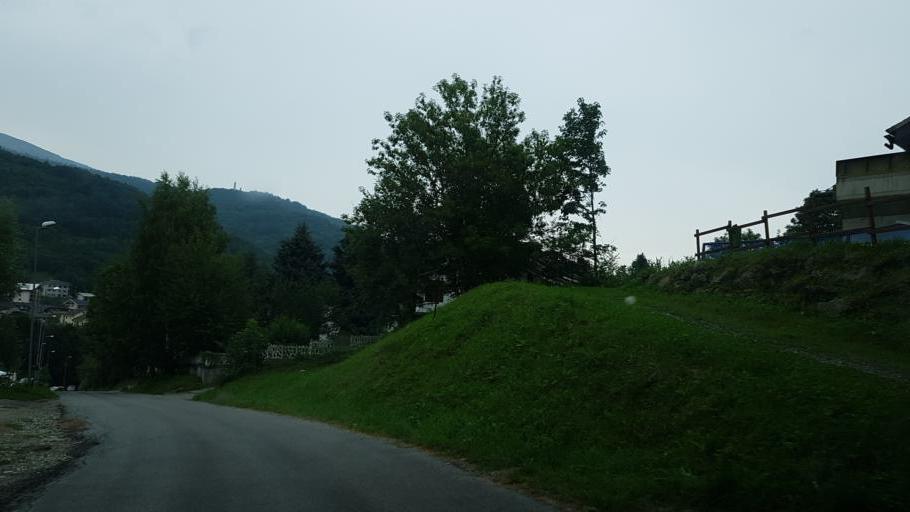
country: IT
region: Piedmont
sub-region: Provincia di Cuneo
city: Sampeyre
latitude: 44.5762
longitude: 7.1804
